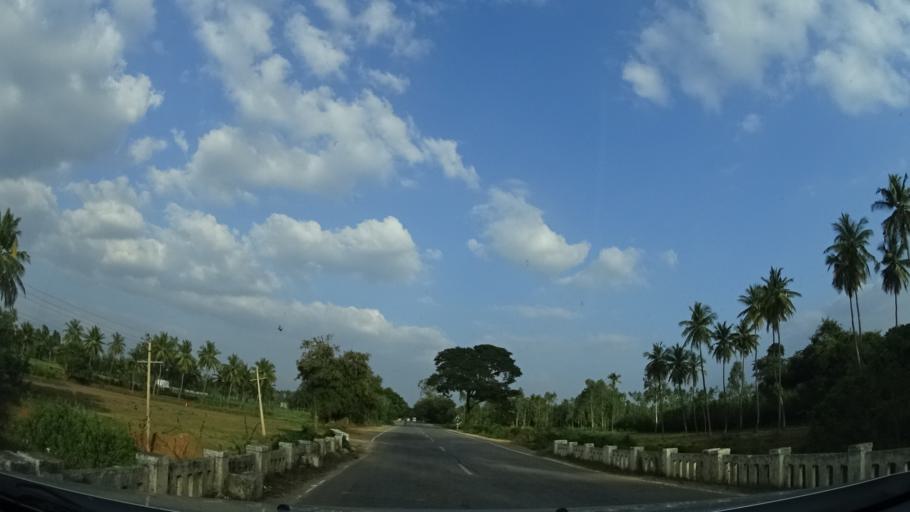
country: IN
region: Karnataka
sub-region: Mandya
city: Malavalli
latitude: 12.3674
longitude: 77.0014
